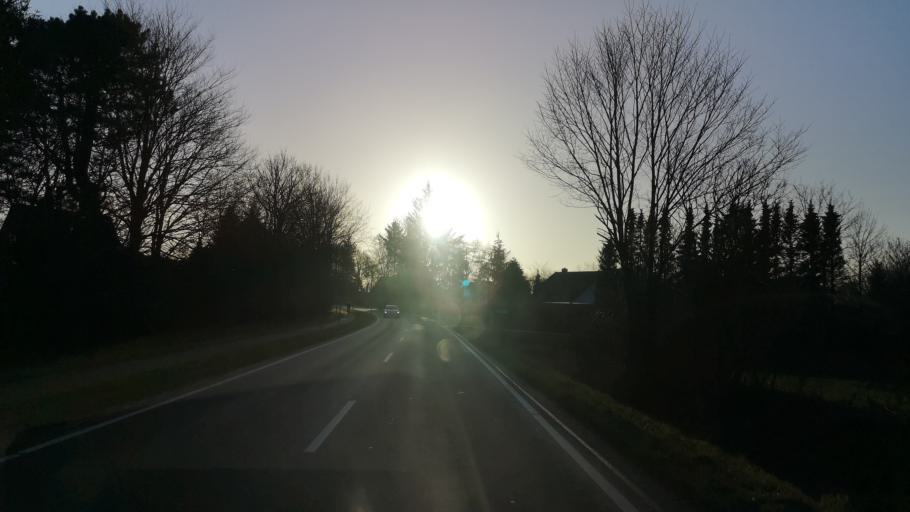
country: DE
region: Schleswig-Holstein
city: Grosssolt
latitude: 54.7014
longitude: 9.5190
